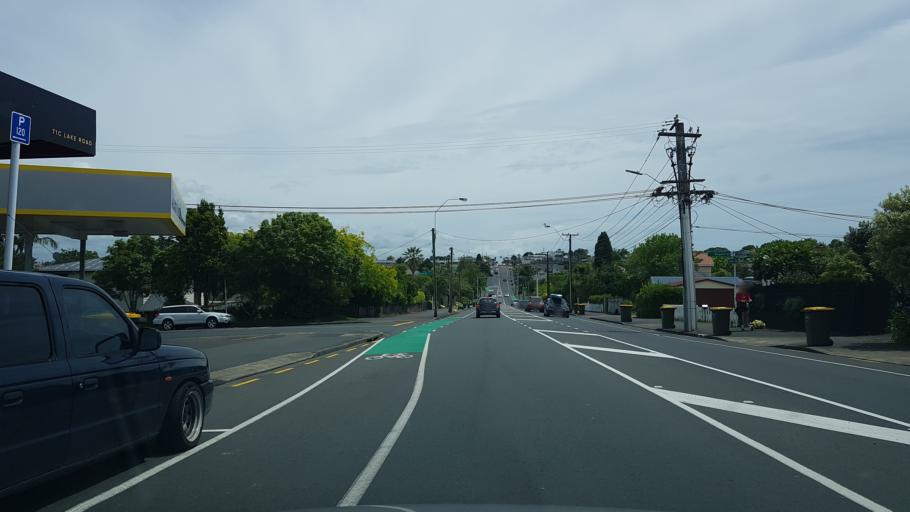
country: NZ
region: Auckland
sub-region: Auckland
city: North Shore
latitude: -36.8127
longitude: 174.7922
